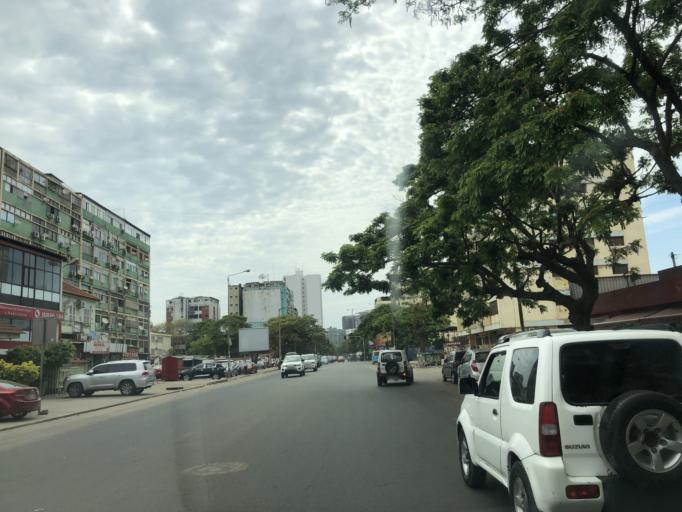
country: AO
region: Luanda
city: Luanda
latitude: -8.8231
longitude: 13.2524
